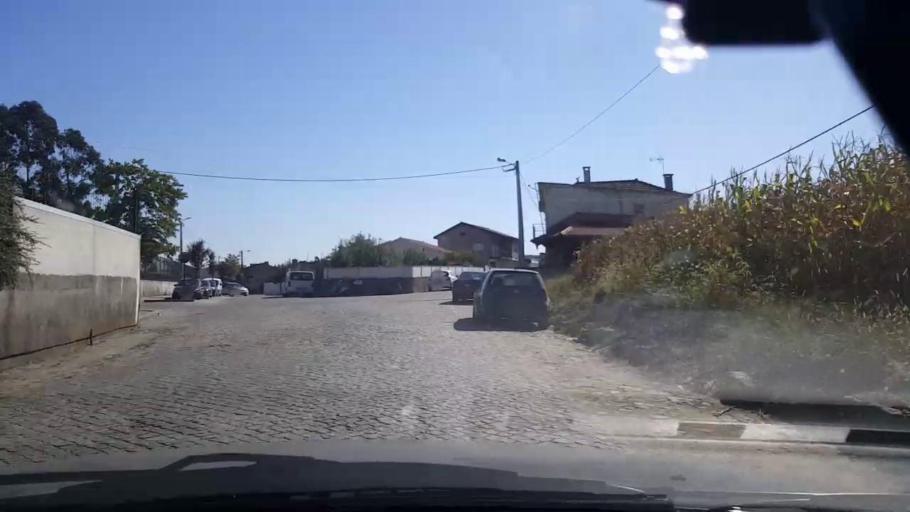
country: PT
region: Braga
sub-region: Vila Nova de Famalicao
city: Ribeirao
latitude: 41.3584
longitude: -8.6263
